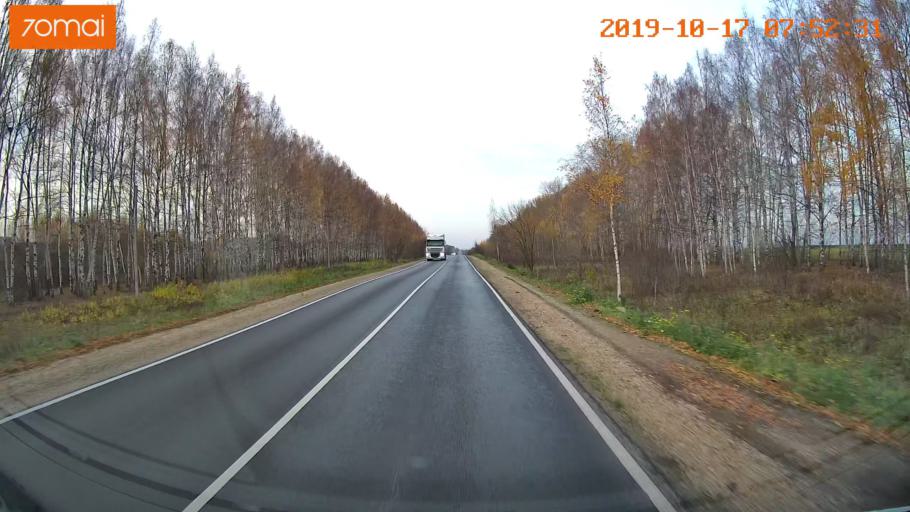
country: RU
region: Vladimir
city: Yur'yev-Pol'skiy
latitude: 56.4718
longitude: 39.6391
